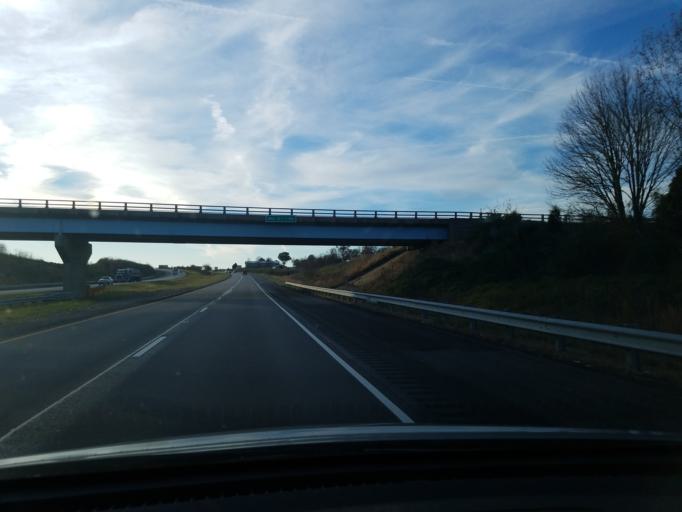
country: US
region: Indiana
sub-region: Dubois County
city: Ferdinand
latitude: 38.1998
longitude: -86.9224
